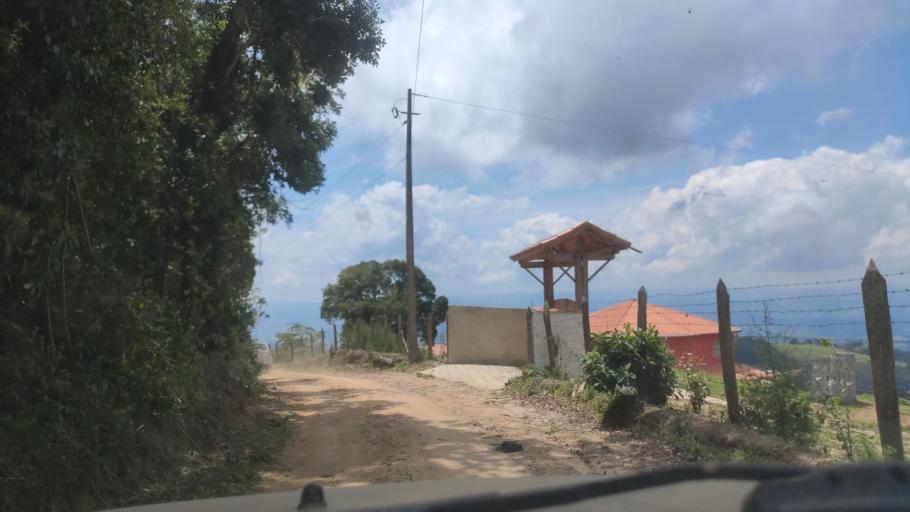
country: BR
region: Minas Gerais
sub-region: Cambui
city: Cambui
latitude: -22.6811
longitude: -45.9614
